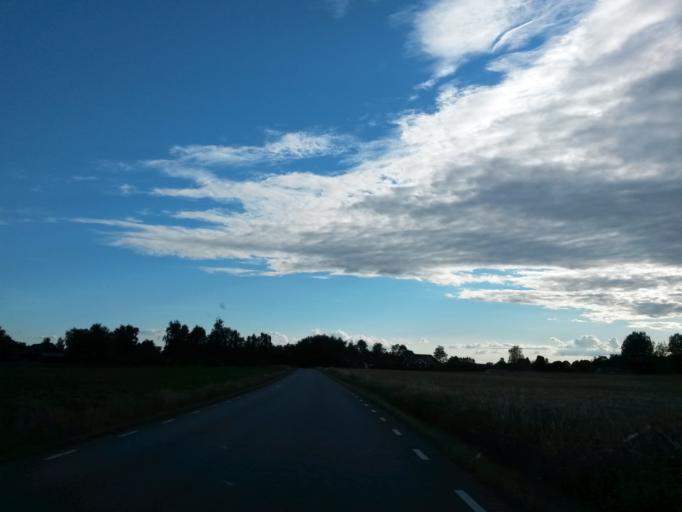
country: SE
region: Vaestra Goetaland
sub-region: Vara Kommun
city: Vara
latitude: 58.2105
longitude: 12.8598
